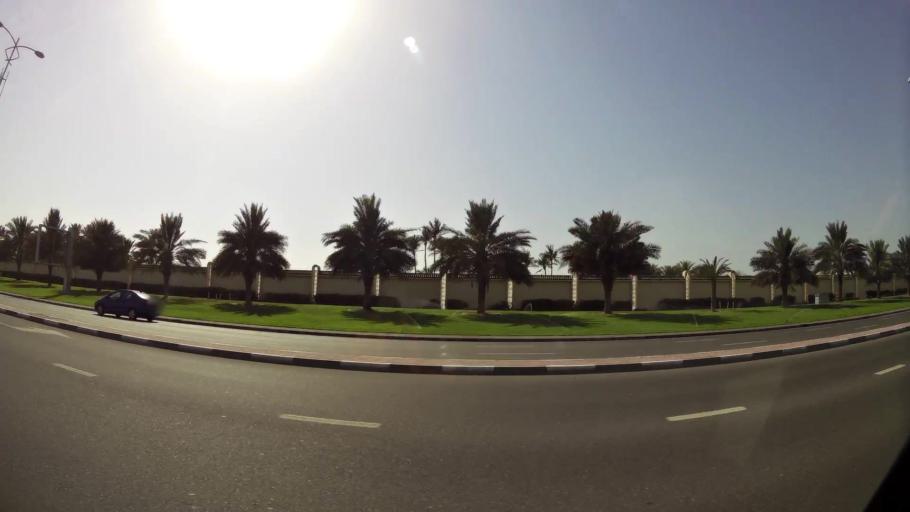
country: AE
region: Dubai
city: Dubai
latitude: 25.1058
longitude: 55.1625
